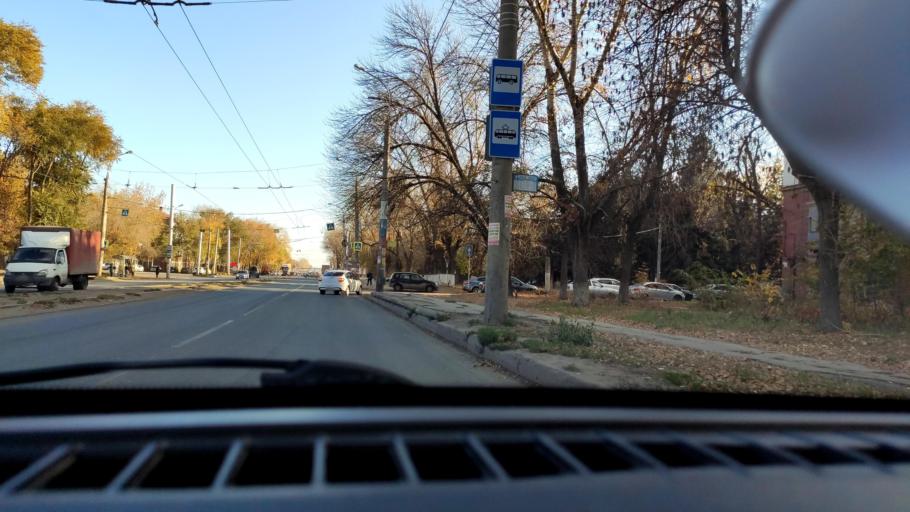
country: RU
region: Samara
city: Smyshlyayevka
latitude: 53.1965
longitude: 50.2894
